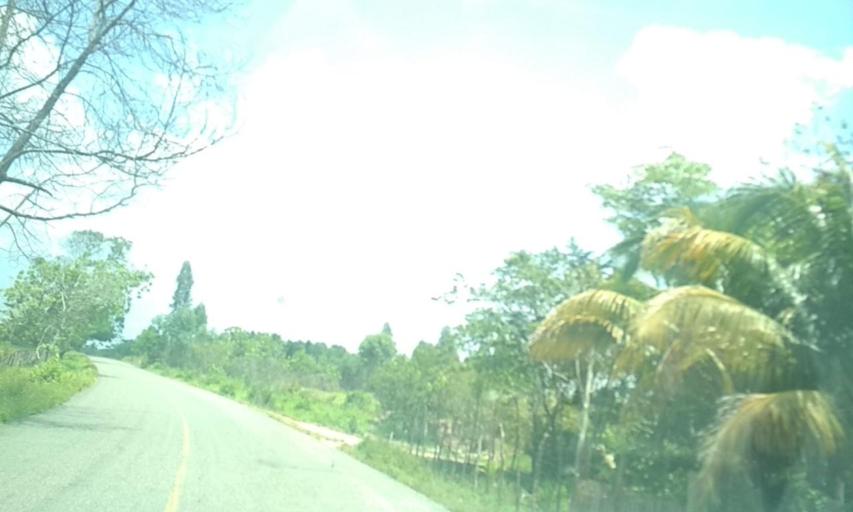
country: MX
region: Tabasco
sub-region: Huimanguillo
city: Francisco Rueda
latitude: 17.7915
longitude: -93.8492
